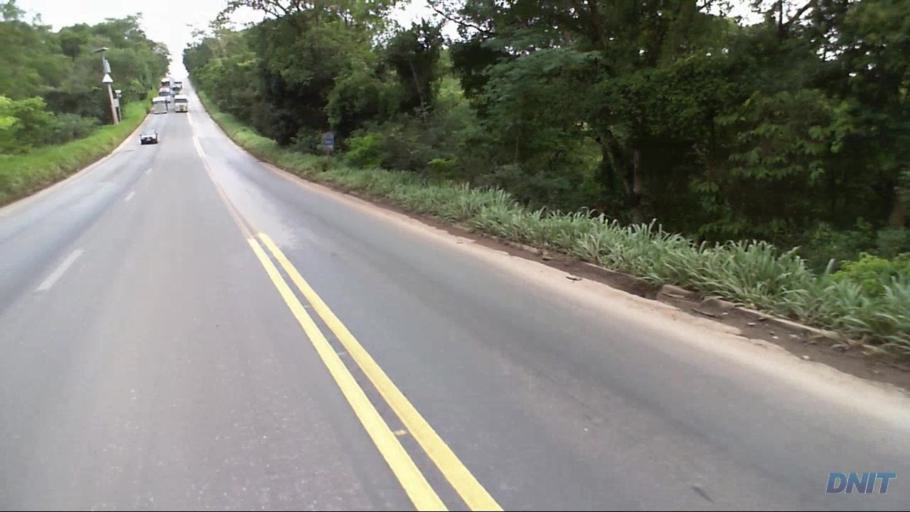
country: BR
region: Goias
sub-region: Uruacu
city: Uruacu
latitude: -14.6032
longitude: -49.1659
